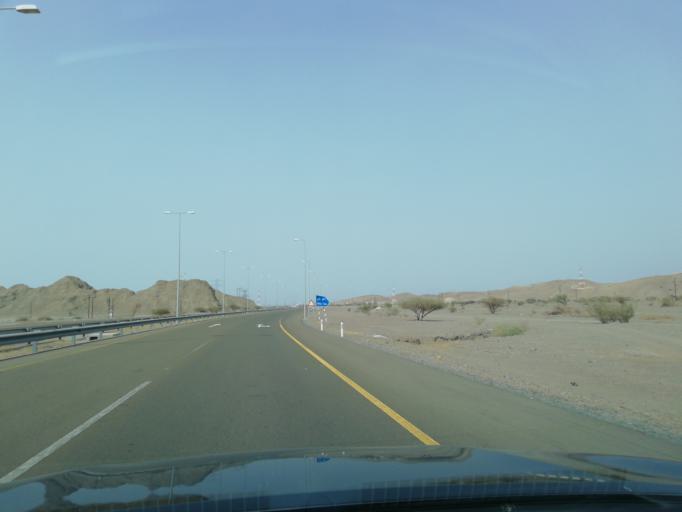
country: OM
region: Al Batinah
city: Al Liwa'
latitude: 24.3472
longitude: 56.5156
